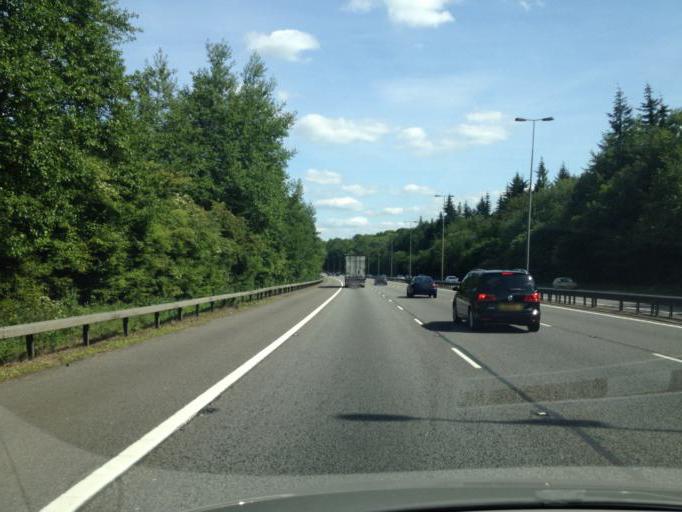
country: GB
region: England
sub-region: Buckinghamshire
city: Stokenchurch
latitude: 51.6337
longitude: -0.8782
